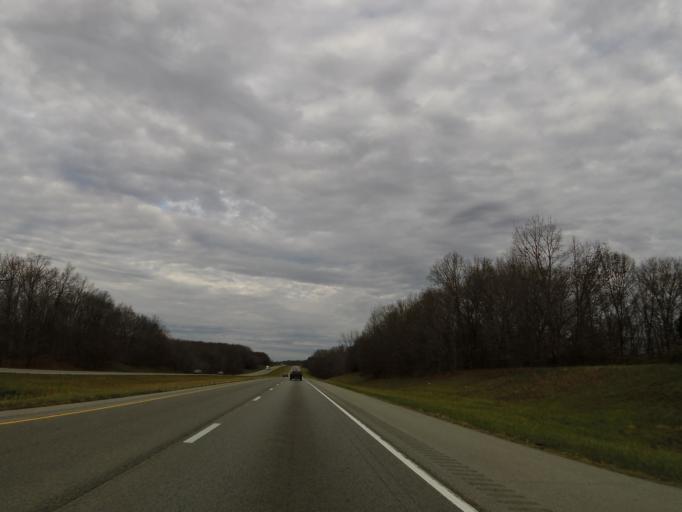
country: US
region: Illinois
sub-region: Clinton County
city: Wamac
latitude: 38.3678
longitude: -89.0904
